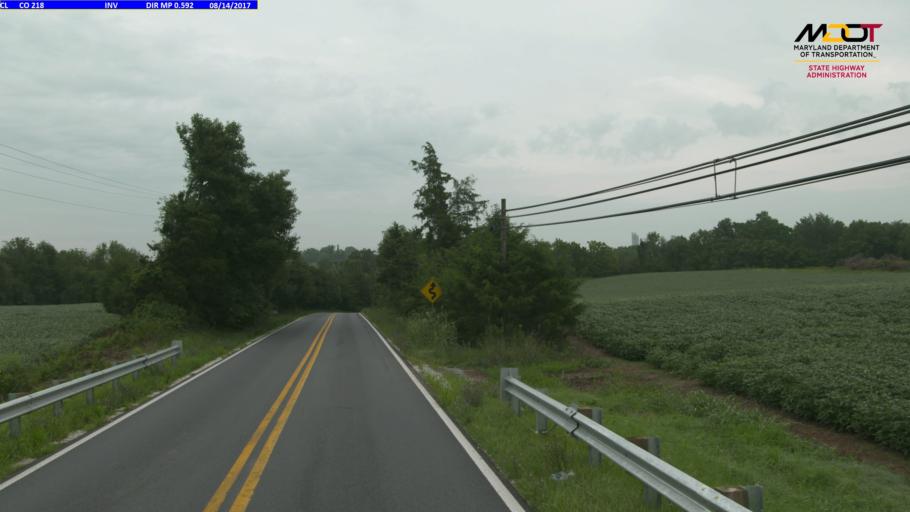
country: US
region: Maryland
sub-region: Carroll County
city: Taneytown
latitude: 39.5868
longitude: -77.1803
